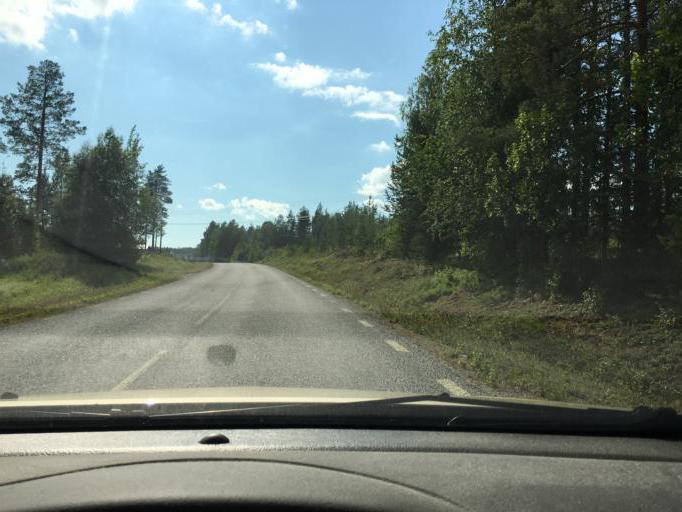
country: SE
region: Norrbotten
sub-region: Kalix Kommun
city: Toere
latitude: 66.0678
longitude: 22.6851
